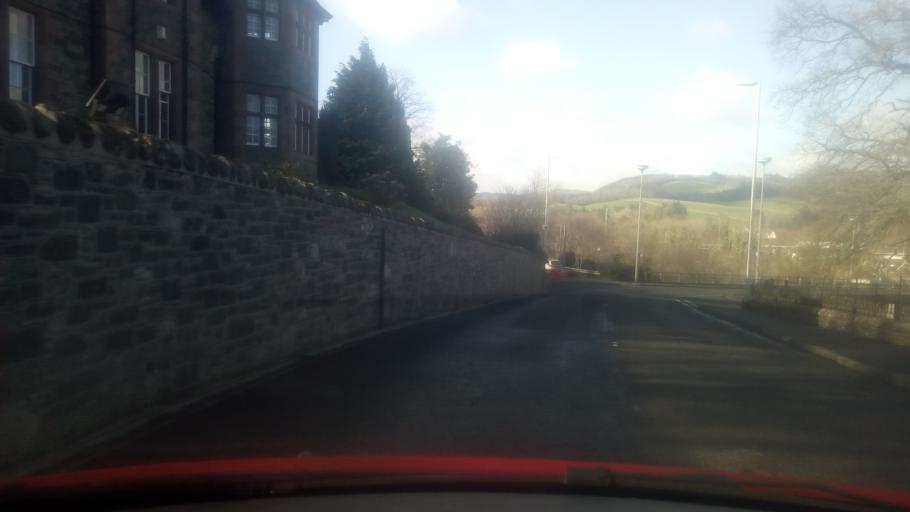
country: GB
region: Scotland
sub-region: The Scottish Borders
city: Selkirk
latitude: 55.5470
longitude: -2.8520
